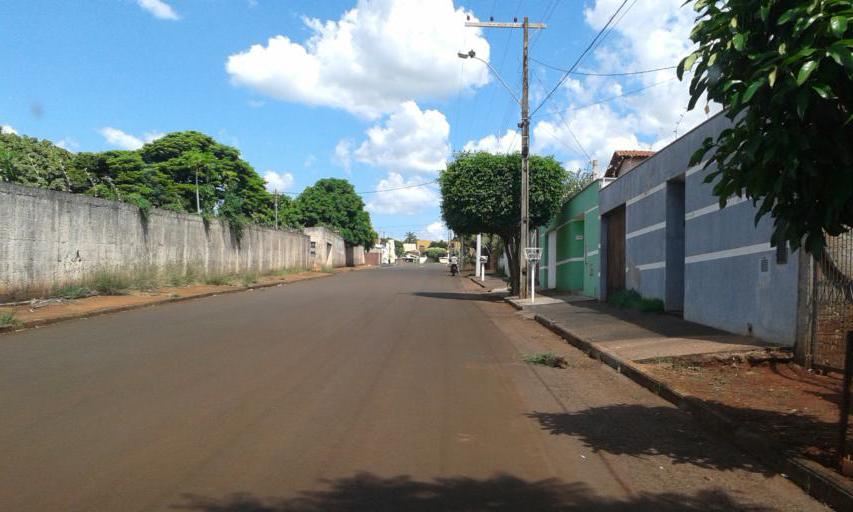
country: BR
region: Minas Gerais
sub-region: Ituiutaba
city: Ituiutaba
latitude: -18.9698
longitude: -49.4799
